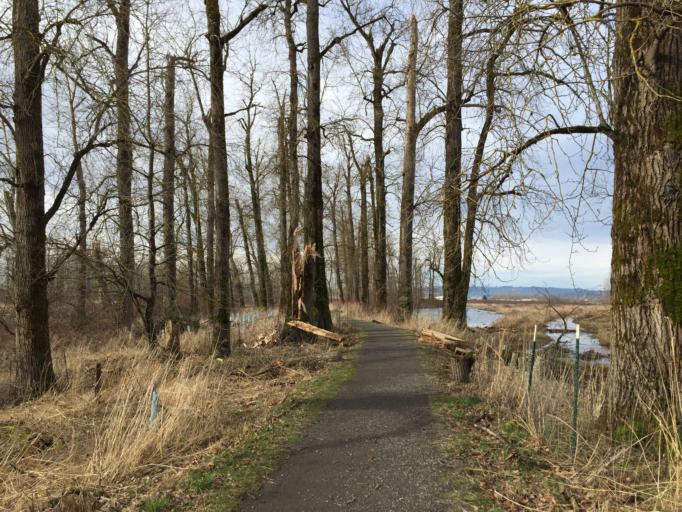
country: US
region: Washington
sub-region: Clark County
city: Washougal
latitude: 45.5629
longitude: -122.3124
